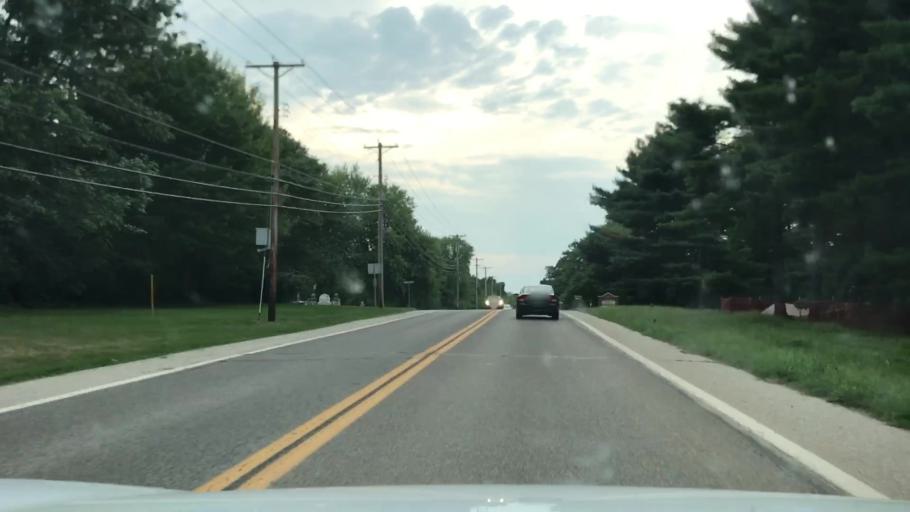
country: US
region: Missouri
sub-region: Saint Louis County
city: Chesterfield
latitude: 38.6552
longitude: -90.6063
